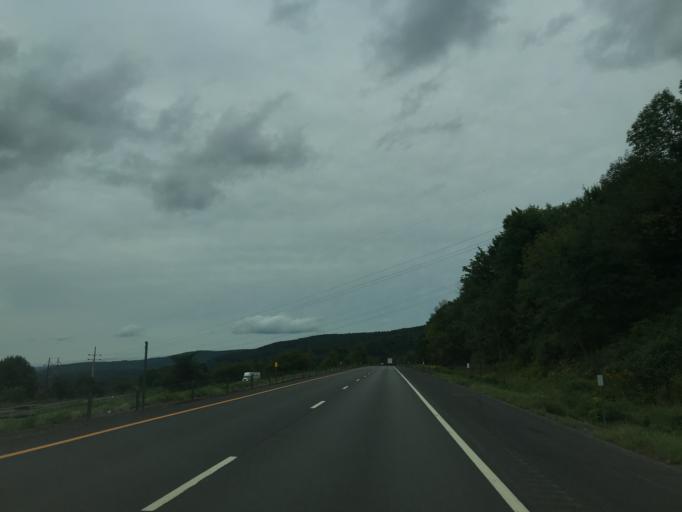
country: US
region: New York
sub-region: Chenango County
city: Bainbridge
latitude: 42.2927
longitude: -75.4533
